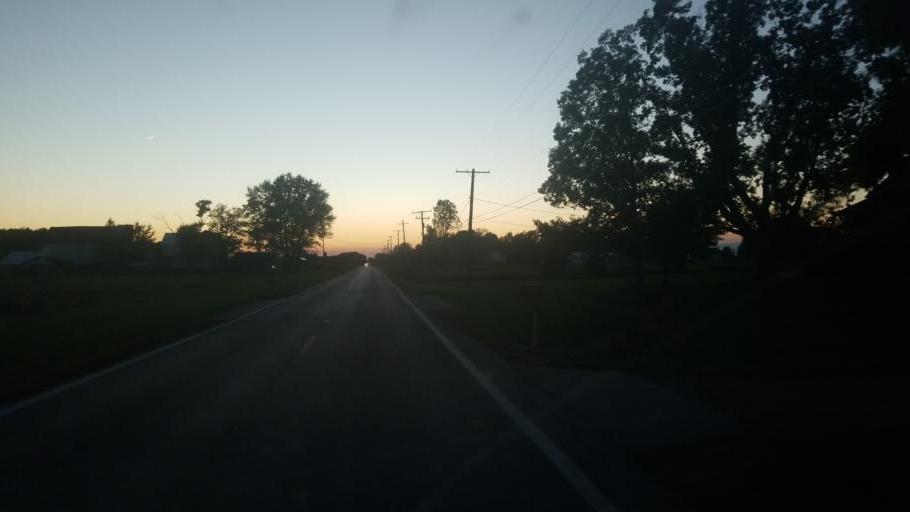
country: US
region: Ohio
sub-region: Ashtabula County
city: Jefferson
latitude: 41.7518
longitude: -80.6531
